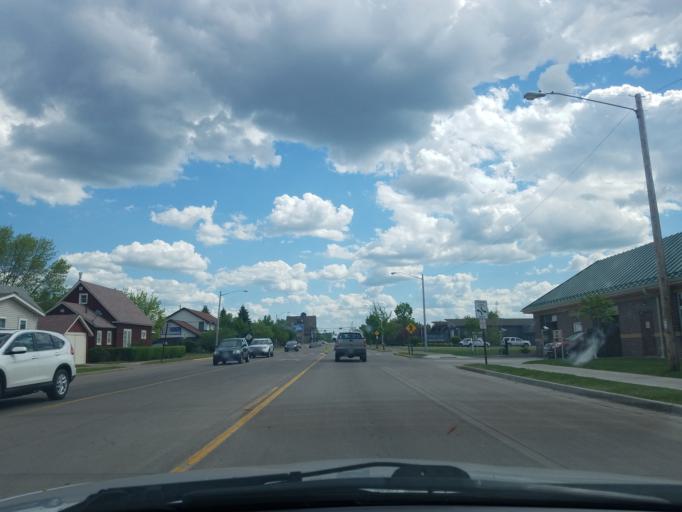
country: US
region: Wisconsin
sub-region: Douglas County
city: Superior
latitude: 46.7308
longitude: -92.0979
